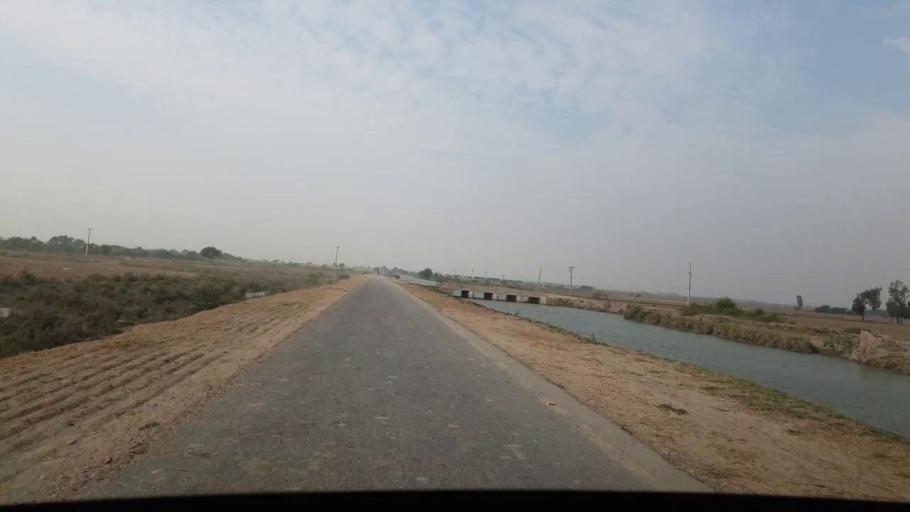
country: PK
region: Sindh
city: Chuhar Jamali
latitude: 24.3952
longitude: 67.9662
